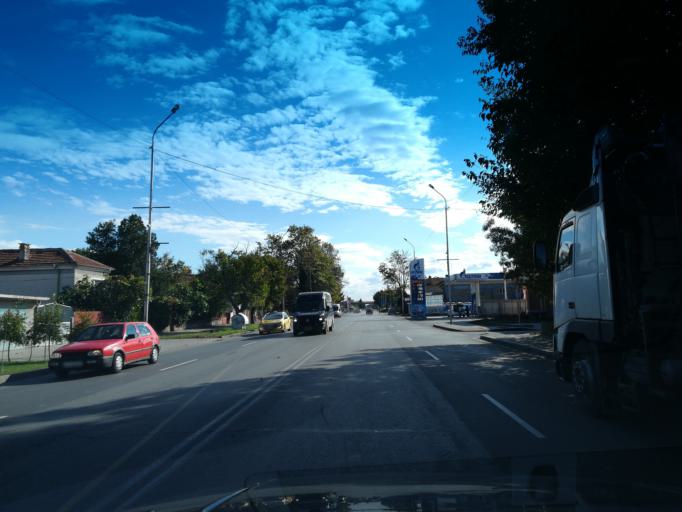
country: BG
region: Stara Zagora
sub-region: Obshtina Stara Zagora
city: Stara Zagora
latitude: 42.3976
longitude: 25.6447
